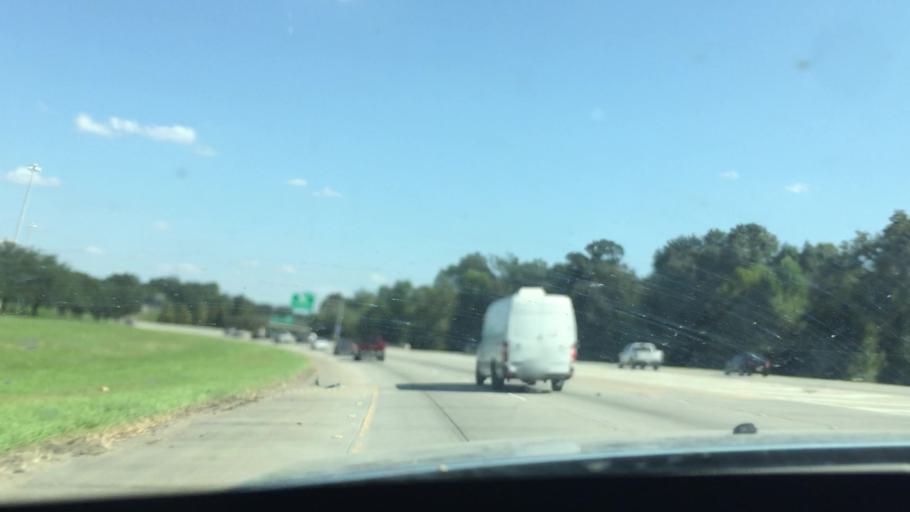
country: US
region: Louisiana
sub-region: East Baton Rouge Parish
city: Westminster
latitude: 30.4189
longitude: -91.1198
